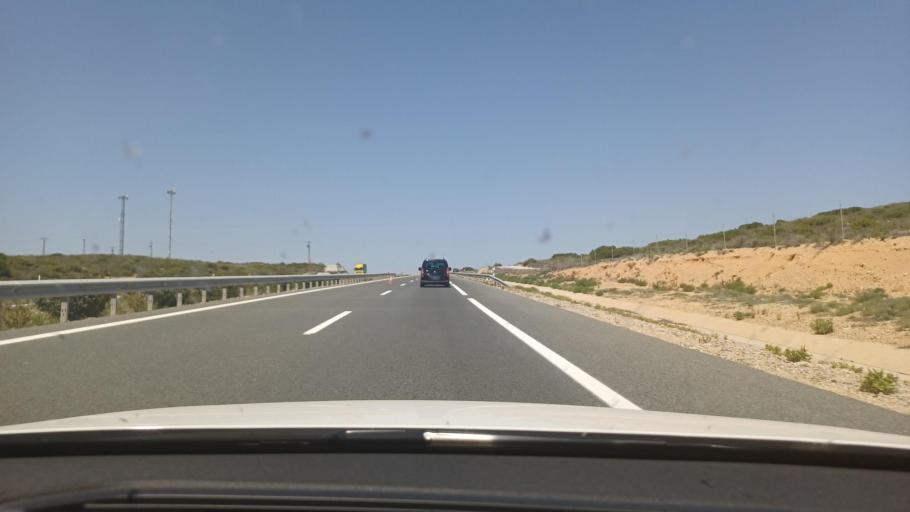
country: ES
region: Castille-La Mancha
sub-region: Provincia de Albacete
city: Alpera
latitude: 38.8785
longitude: -1.1964
